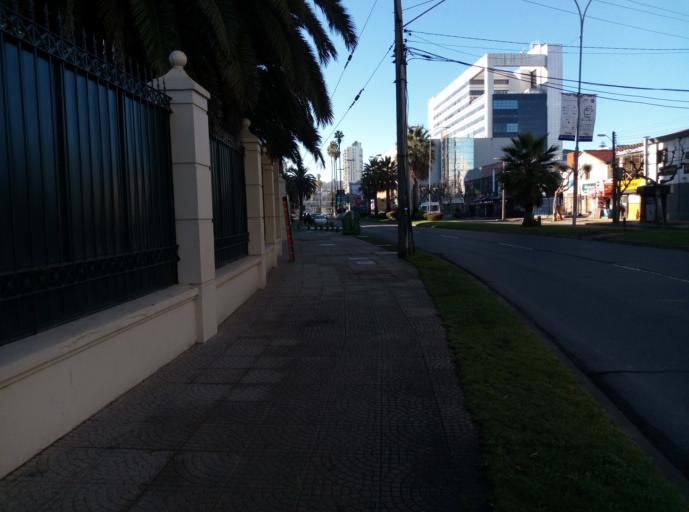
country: CL
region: Valparaiso
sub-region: Provincia de Valparaiso
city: Vina del Mar
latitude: -33.0077
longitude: -71.5500
